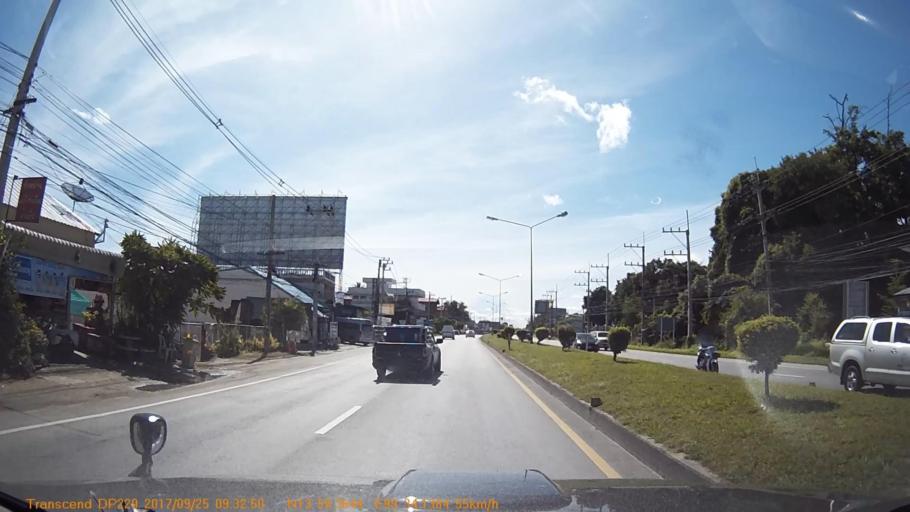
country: TH
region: Kanchanaburi
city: Kanchanaburi
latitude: 13.9893
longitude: 99.5692
